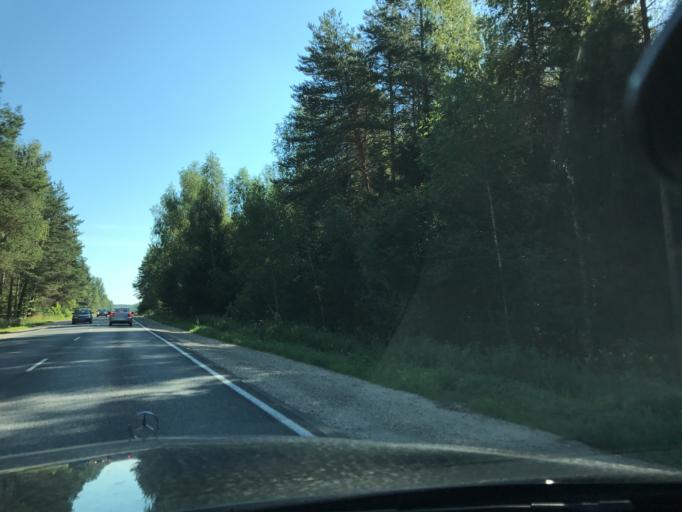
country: RU
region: Vladimir
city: Kirzhach
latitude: 56.1401
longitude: 38.8136
